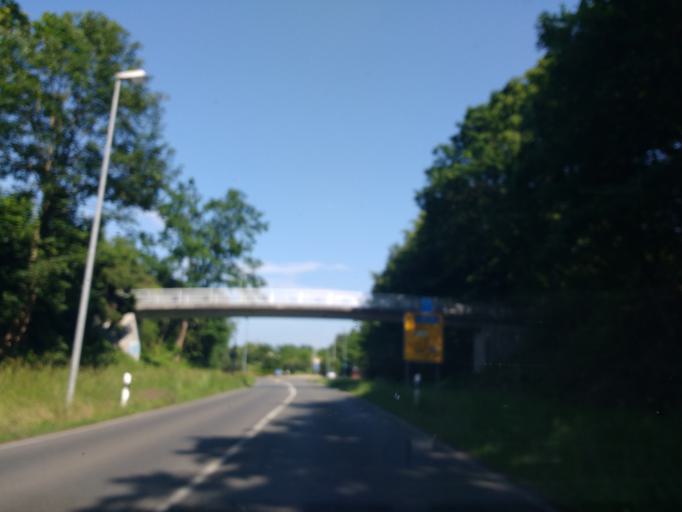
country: DE
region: Hesse
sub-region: Regierungsbezirk Kassel
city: Baunatal
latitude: 51.2588
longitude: 9.3980
